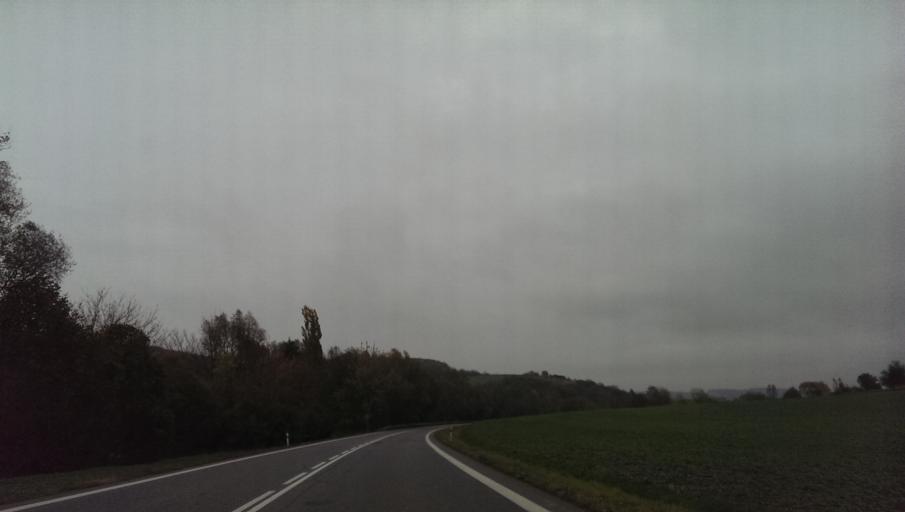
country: CZ
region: South Moravian
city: Nesovice
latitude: 49.1437
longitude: 17.0537
